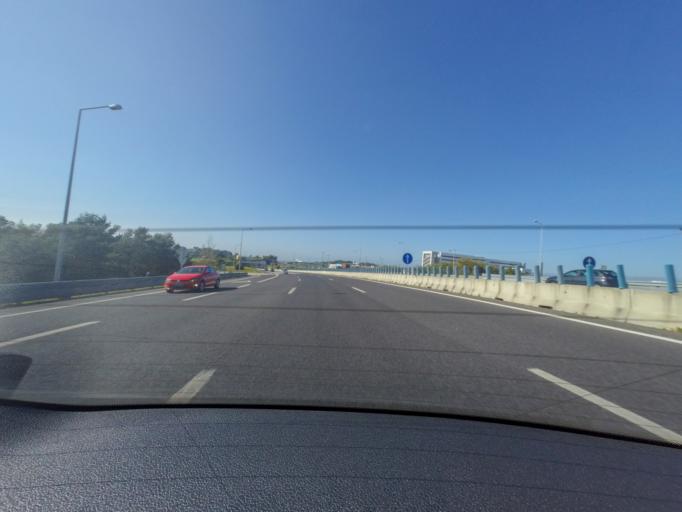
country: PT
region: Lisbon
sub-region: Cascais
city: Alcabideche
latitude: 38.7321
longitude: -9.4156
